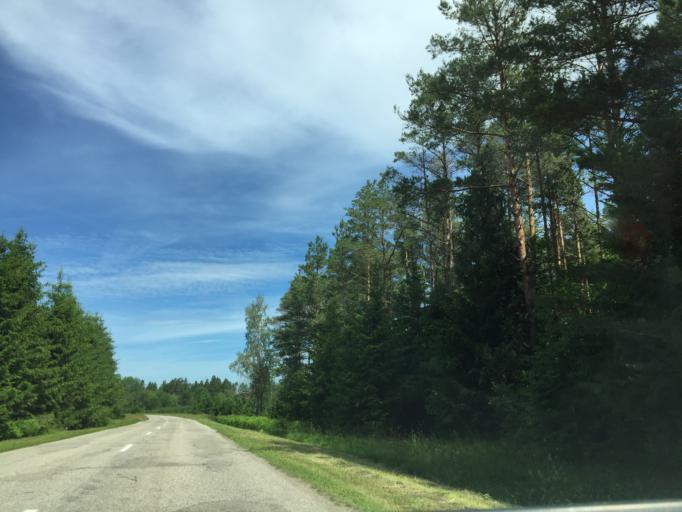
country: LV
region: Dundaga
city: Dundaga
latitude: 57.5765
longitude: 22.3050
